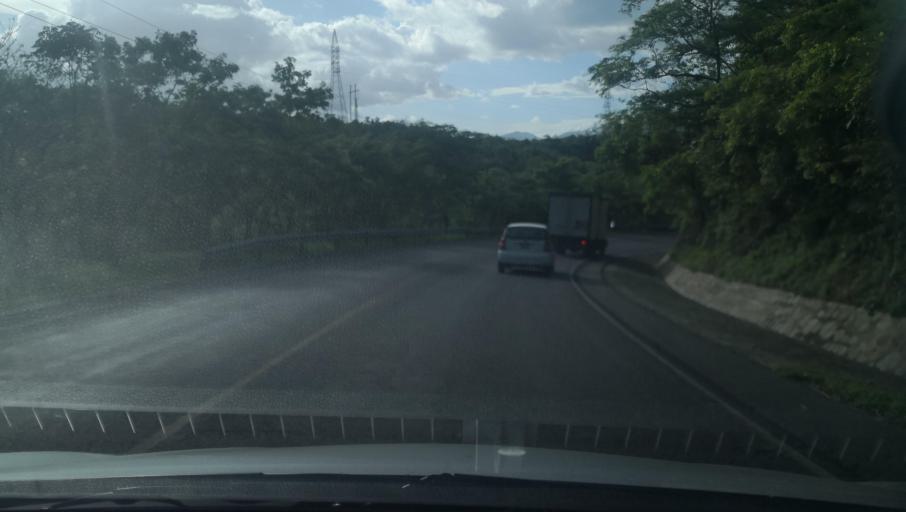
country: NI
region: Nueva Segovia
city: Ocotal
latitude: 13.5989
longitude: -86.4724
